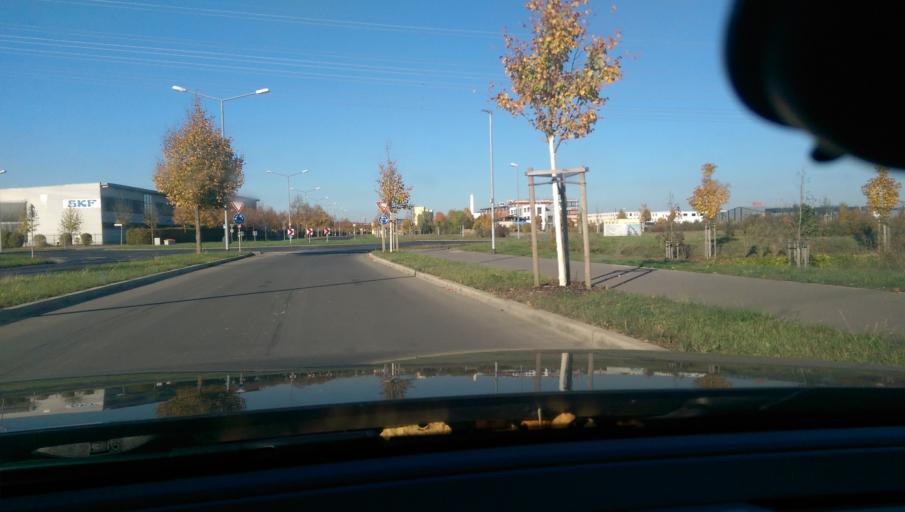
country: DE
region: Bavaria
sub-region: Regierungsbezirk Unterfranken
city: Grafenrheinfeld
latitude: 50.0160
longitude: 10.2147
